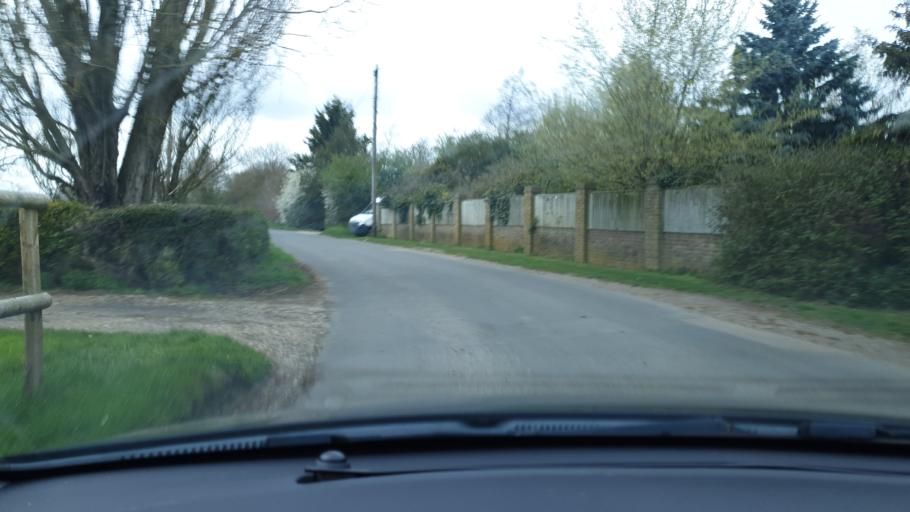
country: GB
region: England
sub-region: Essex
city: Mistley
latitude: 51.9007
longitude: 1.1370
